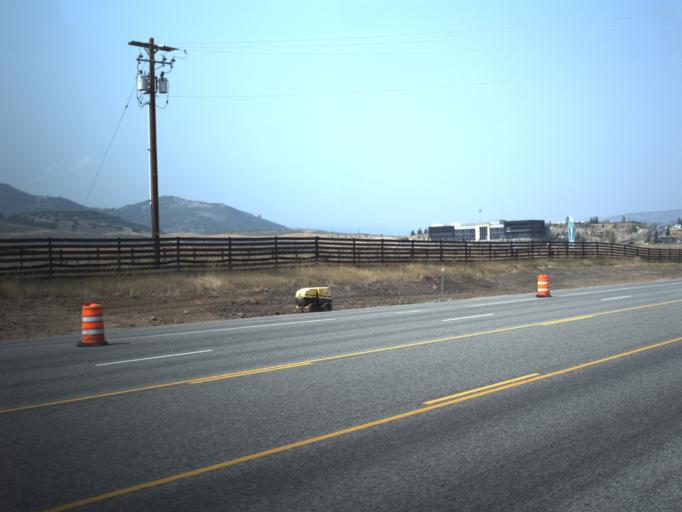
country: US
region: Utah
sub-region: Summit County
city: Snyderville
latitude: 40.7170
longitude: -111.5447
